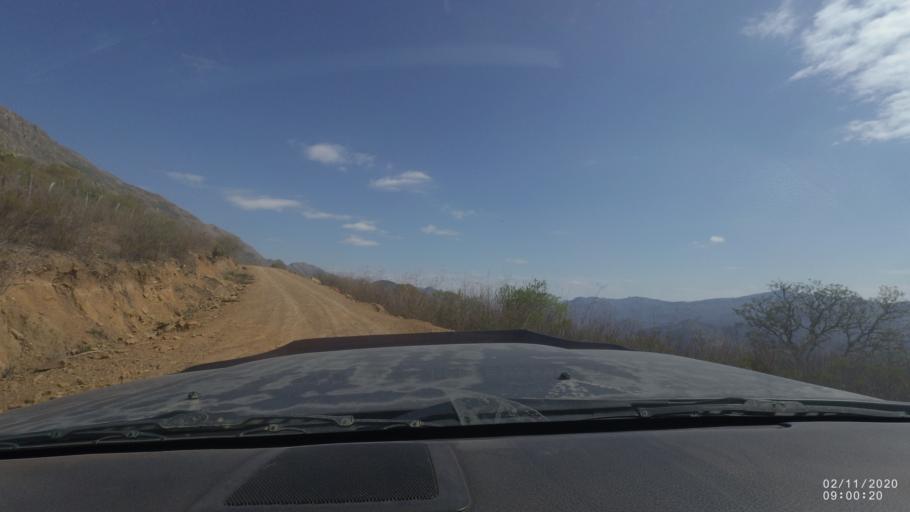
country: BO
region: Chuquisaca
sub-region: Provincia Zudanez
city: Mojocoya
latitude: -18.5435
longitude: -64.5489
